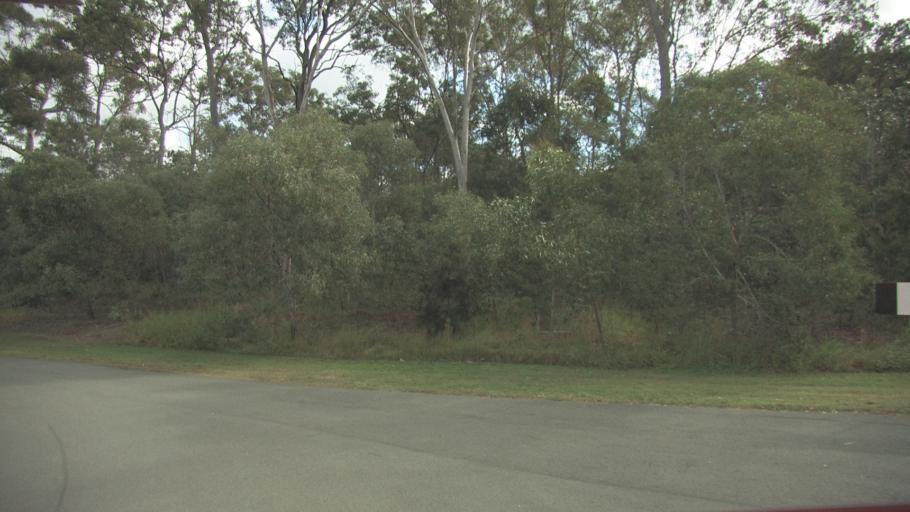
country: AU
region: Queensland
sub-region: Logan
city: Logan Reserve
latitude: -27.6927
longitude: 153.0954
